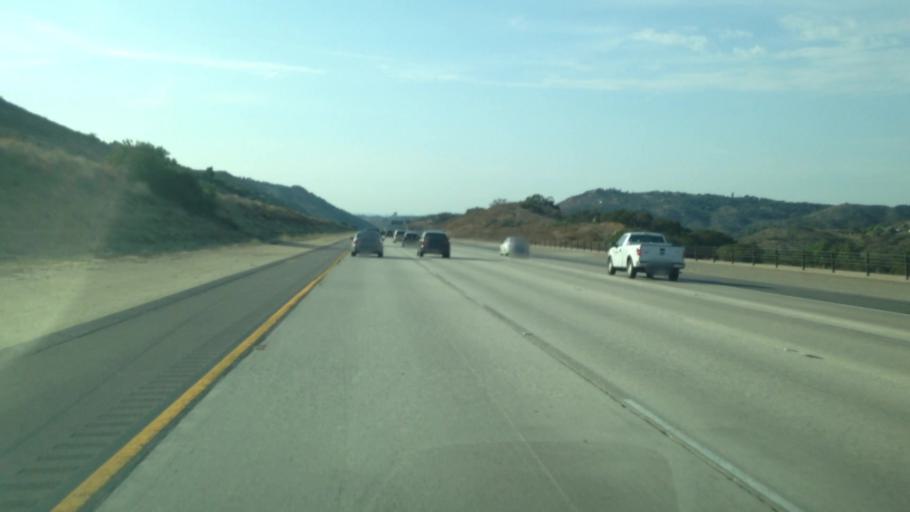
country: US
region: California
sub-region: San Diego County
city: Hidden Meadows
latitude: 33.2344
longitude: -117.1477
